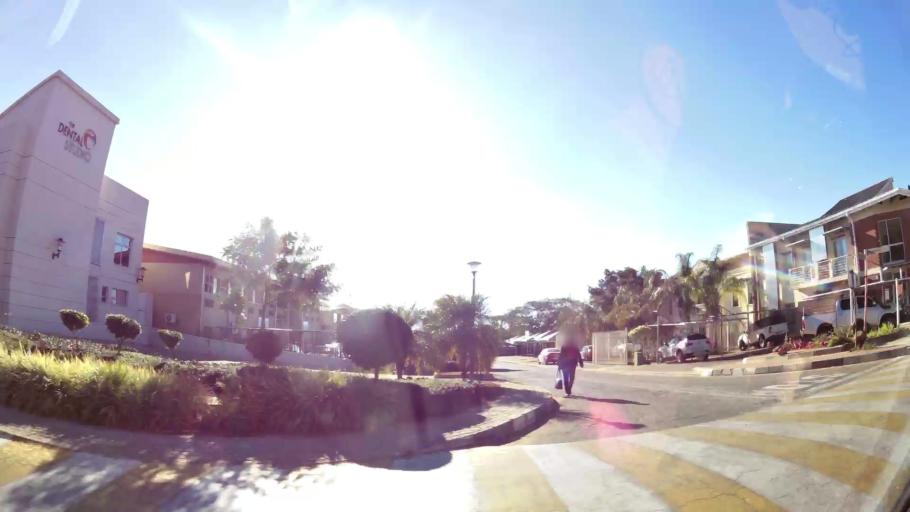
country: ZA
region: Limpopo
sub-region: Capricorn District Municipality
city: Polokwane
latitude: -23.8963
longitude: 29.4803
